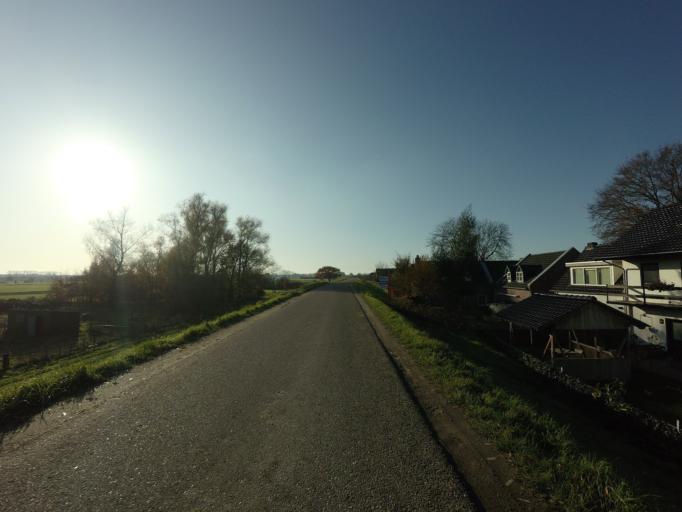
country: NL
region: North Brabant
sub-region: Gemeente 's-Hertogenbosch
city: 's-Hertogenbosch
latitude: 51.7516
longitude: 5.3256
